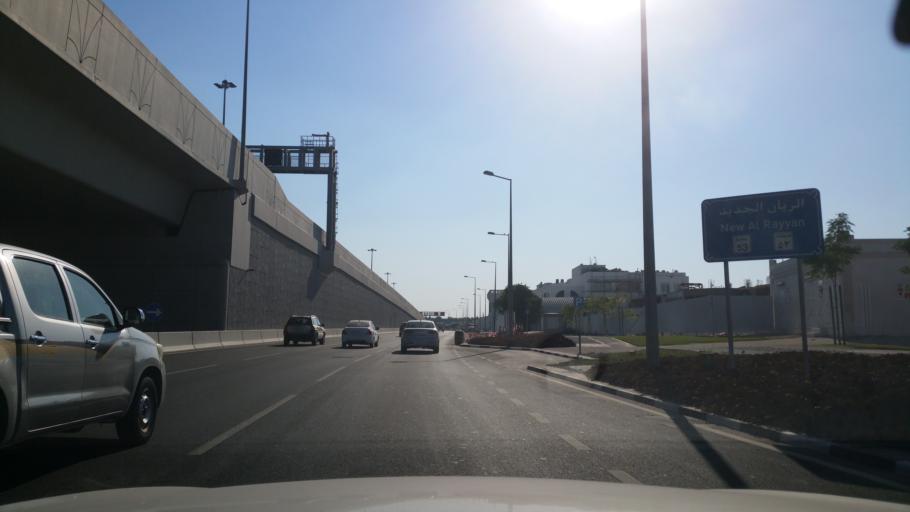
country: QA
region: Baladiyat ar Rayyan
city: Ar Rayyan
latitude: 25.2963
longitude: 51.4456
